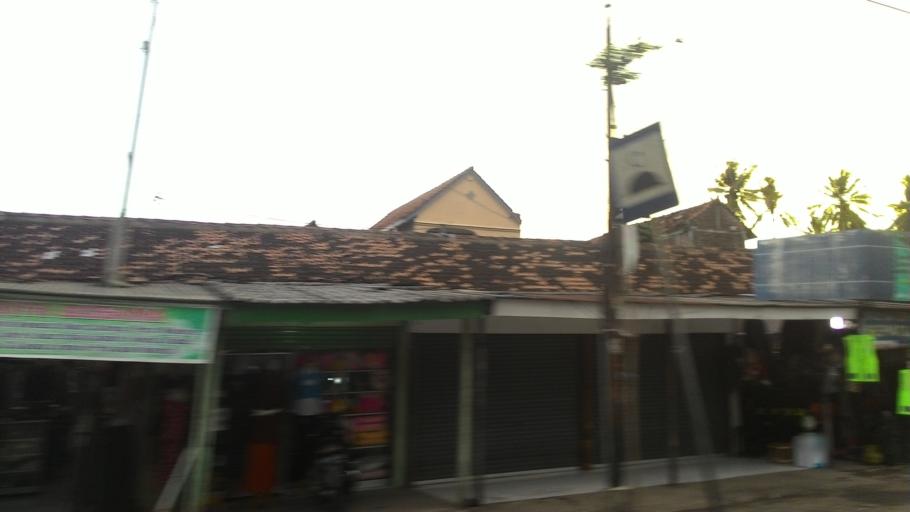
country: ID
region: Daerah Istimewa Yogyakarta
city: Depok
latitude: -7.8274
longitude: 110.4379
